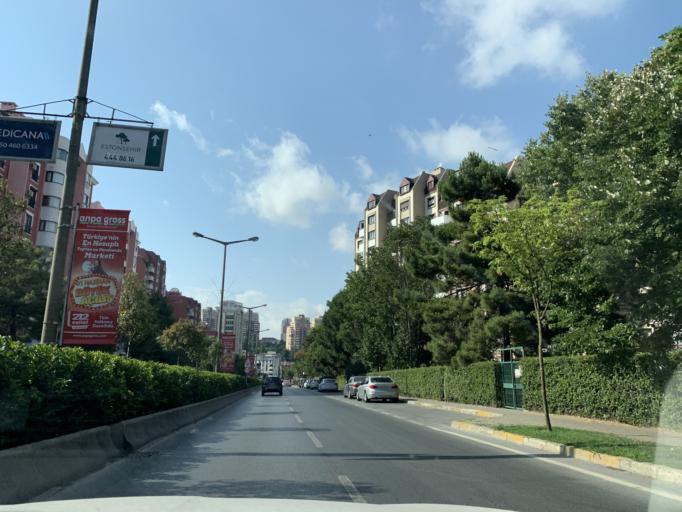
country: TR
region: Istanbul
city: Esenyurt
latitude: 41.0660
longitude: 28.6848
